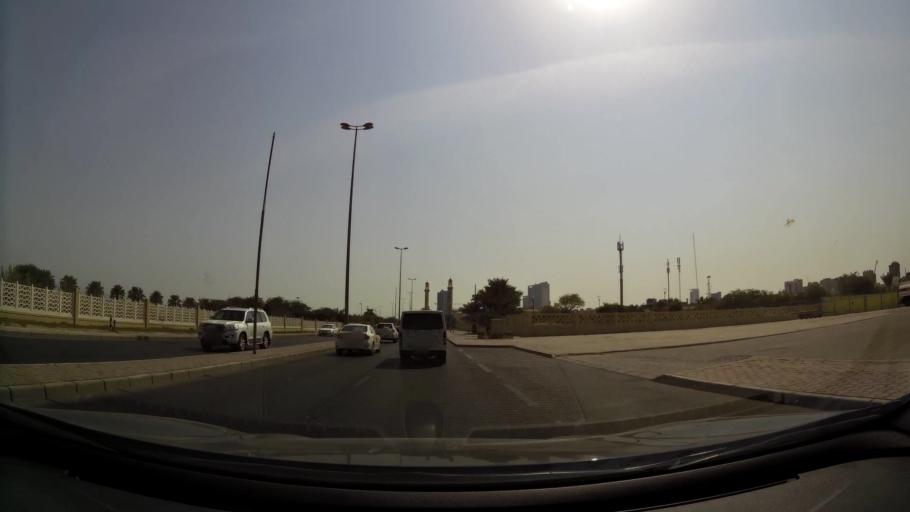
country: KW
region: Al Ahmadi
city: Al Manqaf
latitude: 29.0887
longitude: 48.1380
